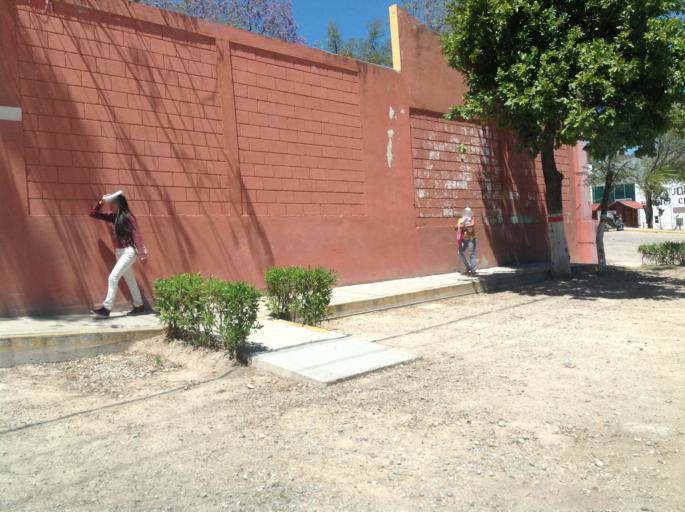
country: MX
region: Oaxaca
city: Ciudad de Huajuapam de Leon
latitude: 17.8143
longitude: -97.7797
